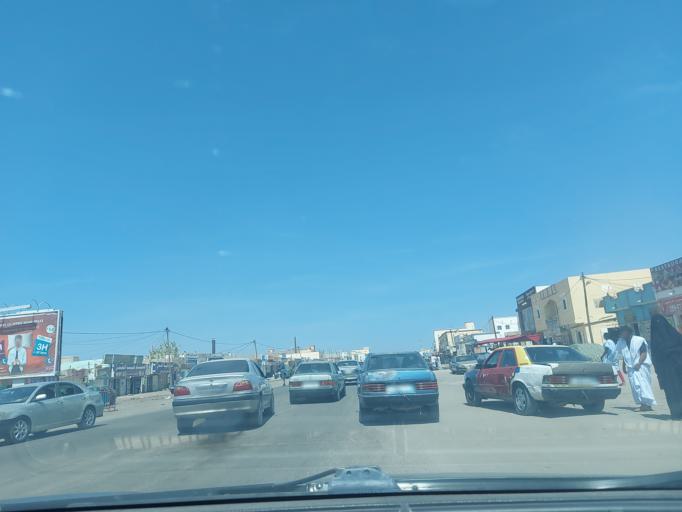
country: MR
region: Nouakchott
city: Nouakchott
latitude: 18.0739
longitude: -15.9458
